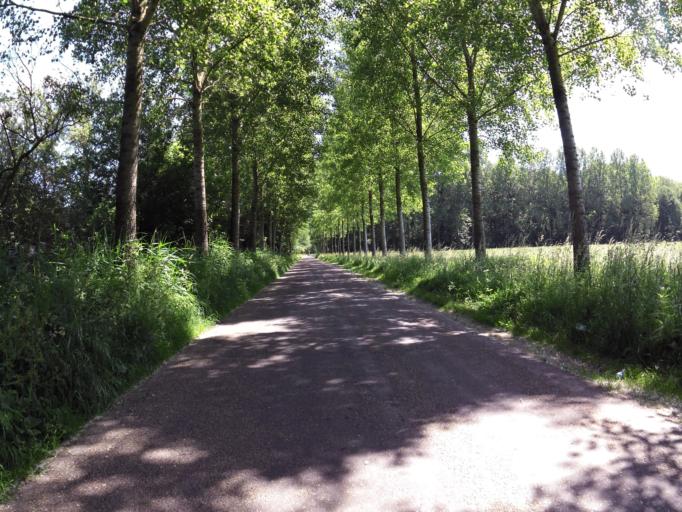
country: NL
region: North Brabant
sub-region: Gemeente Boxtel
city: Boxtel
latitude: 51.5901
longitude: 5.3689
